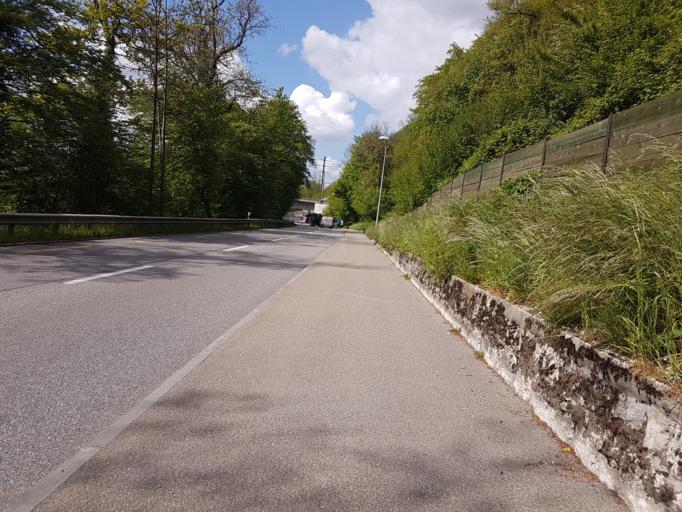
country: CH
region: Aargau
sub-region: Bezirk Zofingen
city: Aarburg
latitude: 47.3190
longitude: 7.8951
